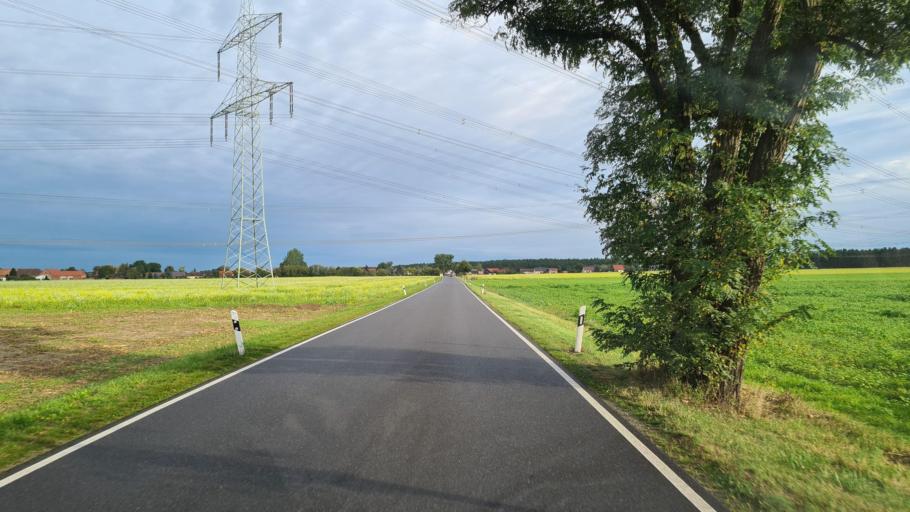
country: DE
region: Brandenburg
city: Kasel-Golzig
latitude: 51.8946
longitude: 13.7154
